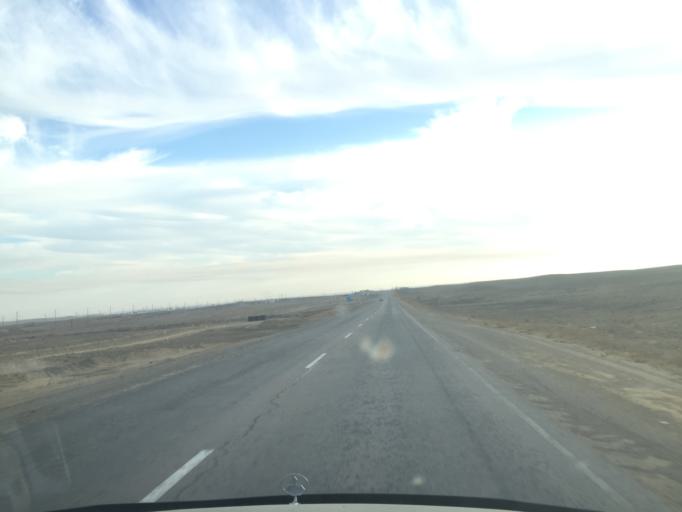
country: KZ
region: Almaty Oblysy
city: Ulken
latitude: 45.1335
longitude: 73.9651
